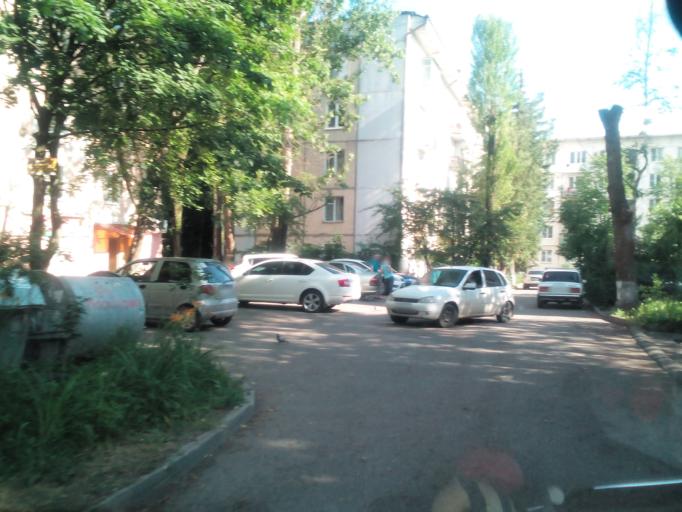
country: RU
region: Stavropol'skiy
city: Pyatigorsk
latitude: 44.0614
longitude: 43.0561
